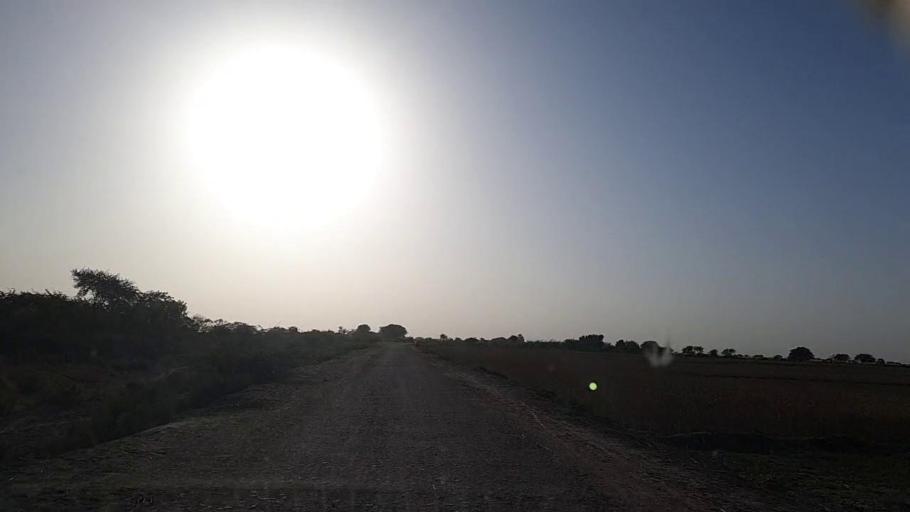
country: PK
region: Sindh
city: Jati
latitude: 24.4167
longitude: 68.3016
